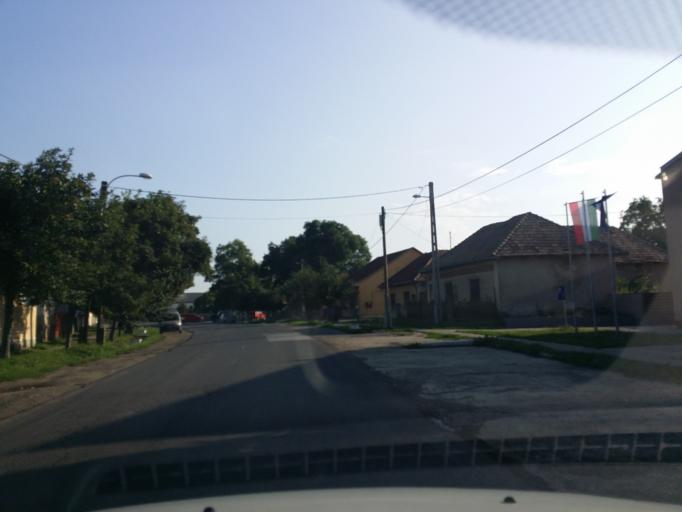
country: HU
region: Borsod-Abauj-Zemplen
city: Encs
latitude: 48.3856
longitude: 21.2167
